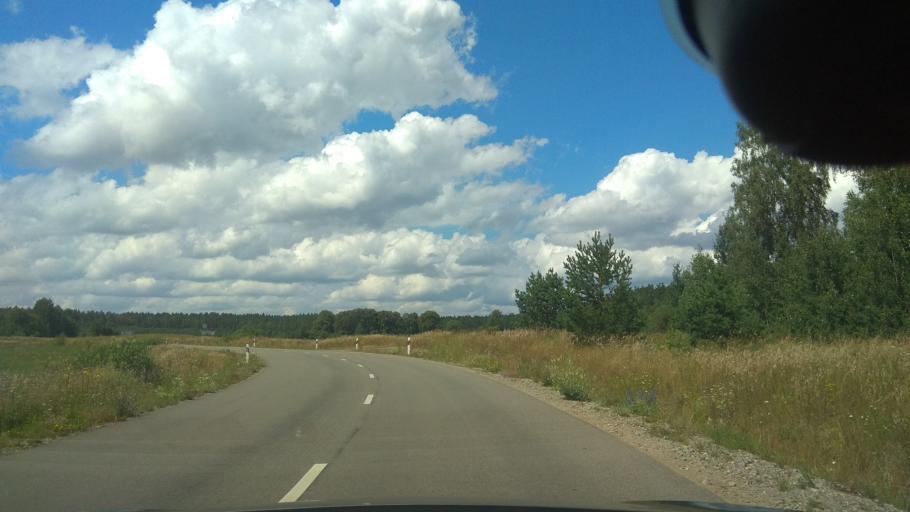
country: LT
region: Vilnius County
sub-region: Trakai
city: Rudiskes
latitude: 54.5104
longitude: 24.8630
